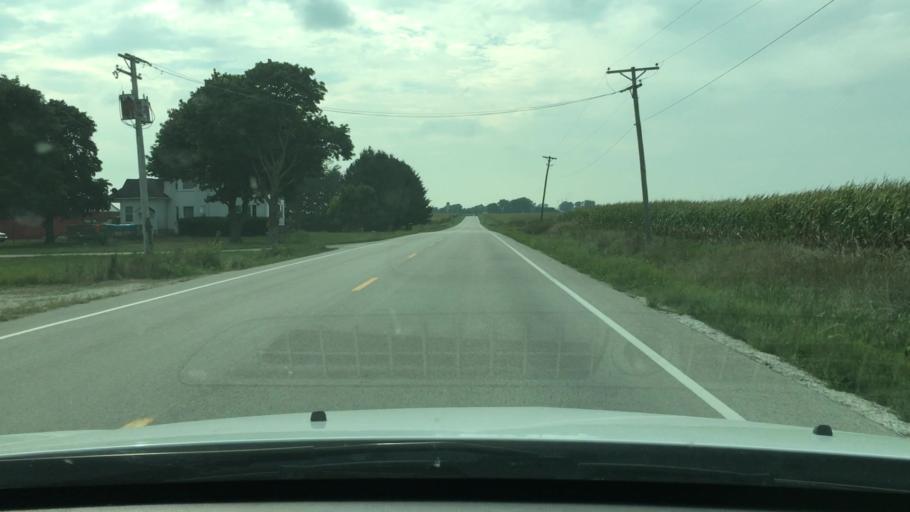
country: US
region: Illinois
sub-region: DeKalb County
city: Malta
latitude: 41.8486
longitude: -88.8584
